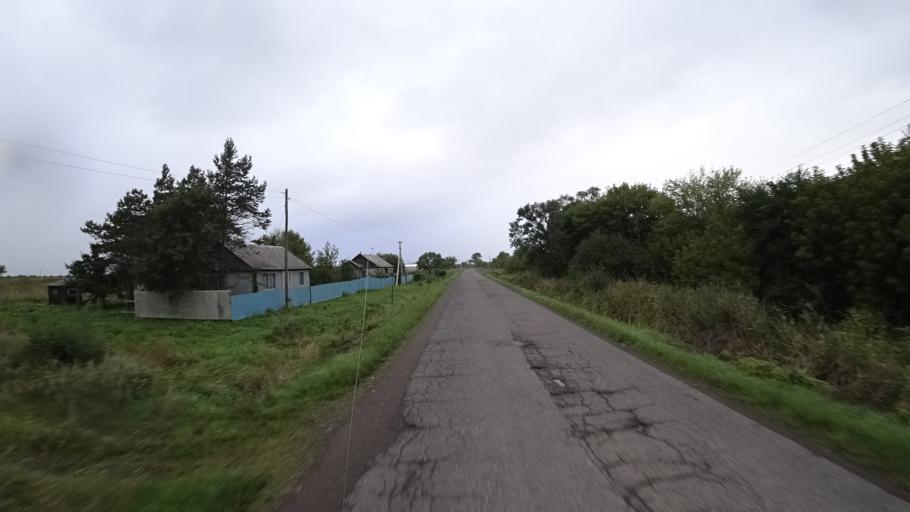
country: RU
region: Primorskiy
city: Chernigovka
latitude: 44.3973
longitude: 132.5278
